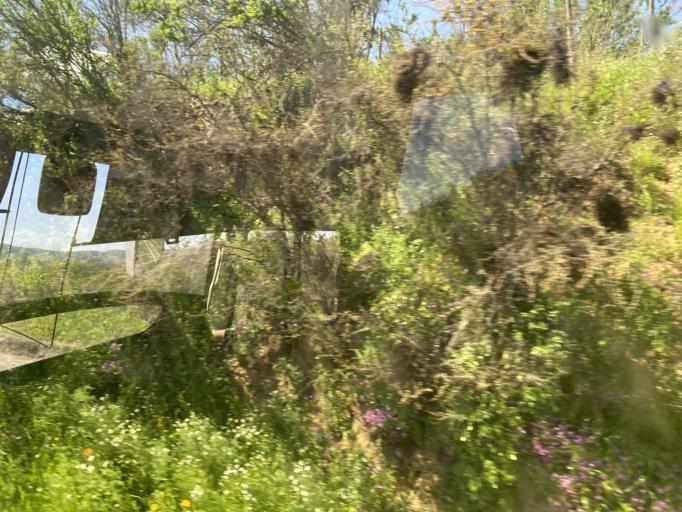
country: CL
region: Valparaiso
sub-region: Provincia de Marga Marga
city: Villa Alemana
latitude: -33.1877
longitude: -71.2961
